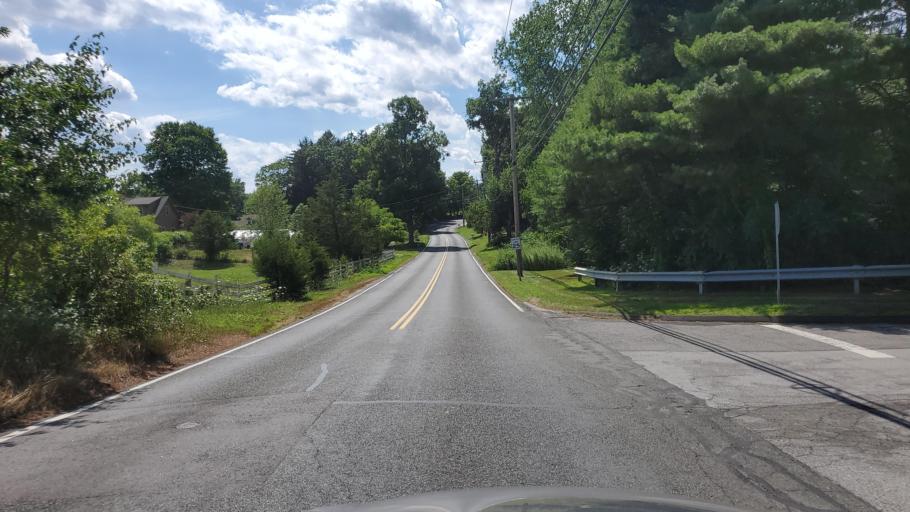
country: US
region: Connecticut
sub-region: Fairfield County
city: Newtown
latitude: 41.3231
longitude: -73.2722
